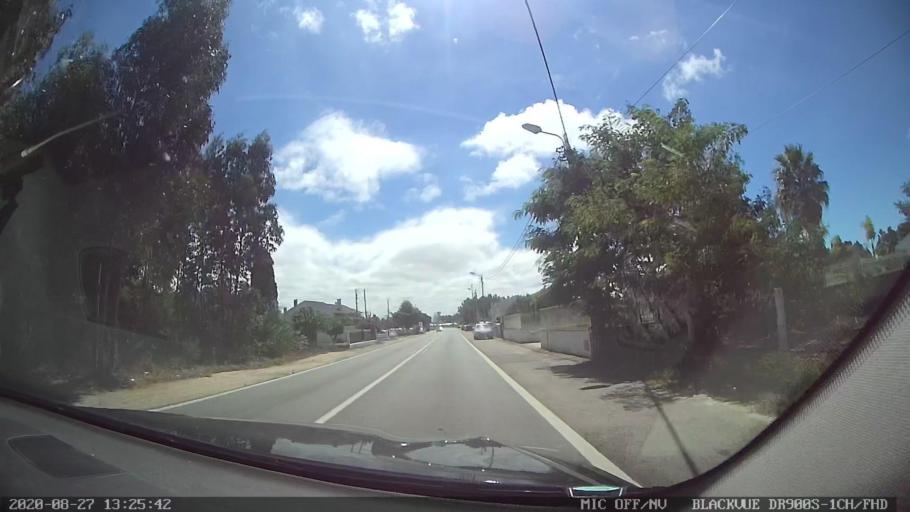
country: PT
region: Aveiro
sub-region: Vagos
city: Vagos
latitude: 40.5442
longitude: -8.6784
